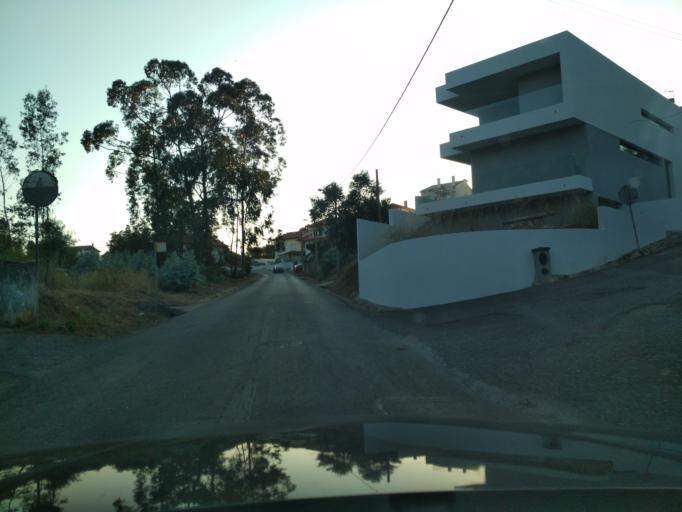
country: PT
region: Coimbra
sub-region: Coimbra
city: Coimbra
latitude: 40.2422
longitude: -8.4021
